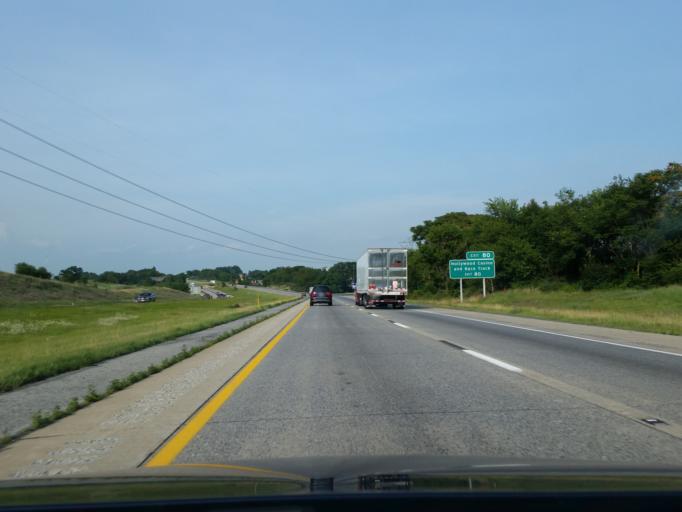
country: US
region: Pennsylvania
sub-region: Dauphin County
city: Skyline View
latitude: 40.3672
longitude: -76.6936
